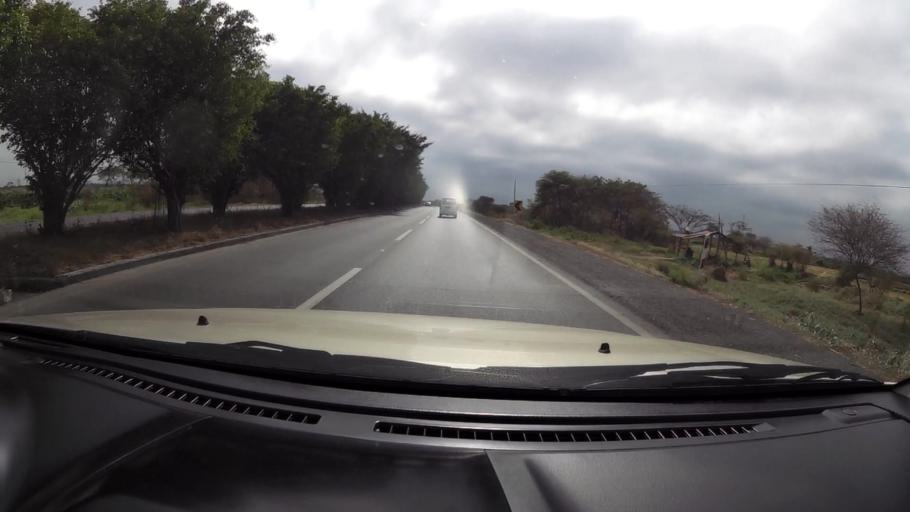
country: EC
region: Guayas
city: Yaguachi Nuevo
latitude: -2.2091
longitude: -79.7359
